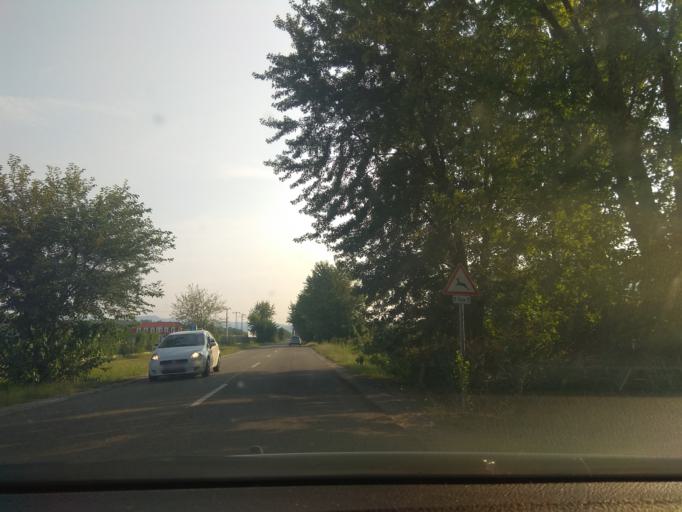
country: HU
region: Heves
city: Eger
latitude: 47.9444
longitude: 20.3787
